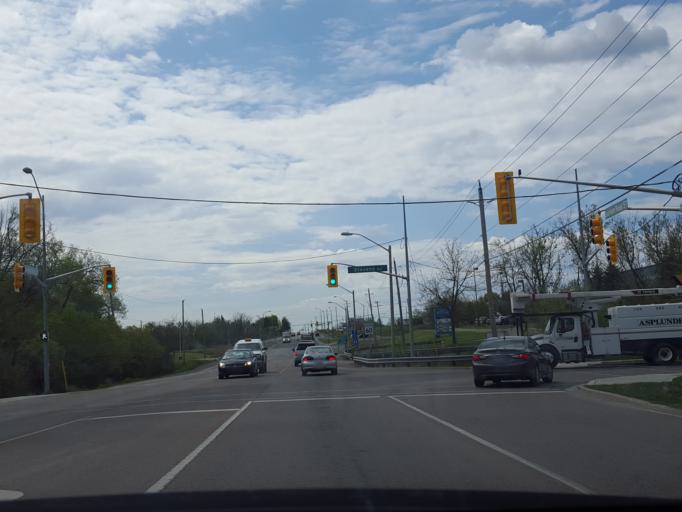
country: CA
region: Ontario
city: Oshawa
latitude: 43.9140
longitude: -78.7031
